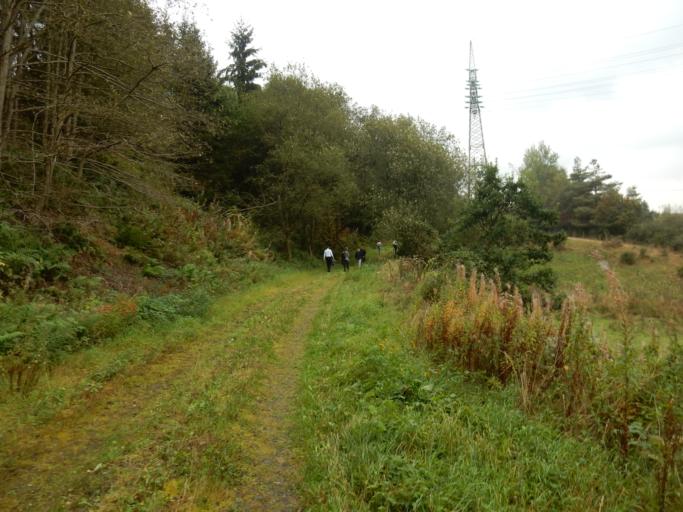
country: LU
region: Diekirch
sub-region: Canton de Wiltz
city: Winseler
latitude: 49.9586
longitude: 5.9113
